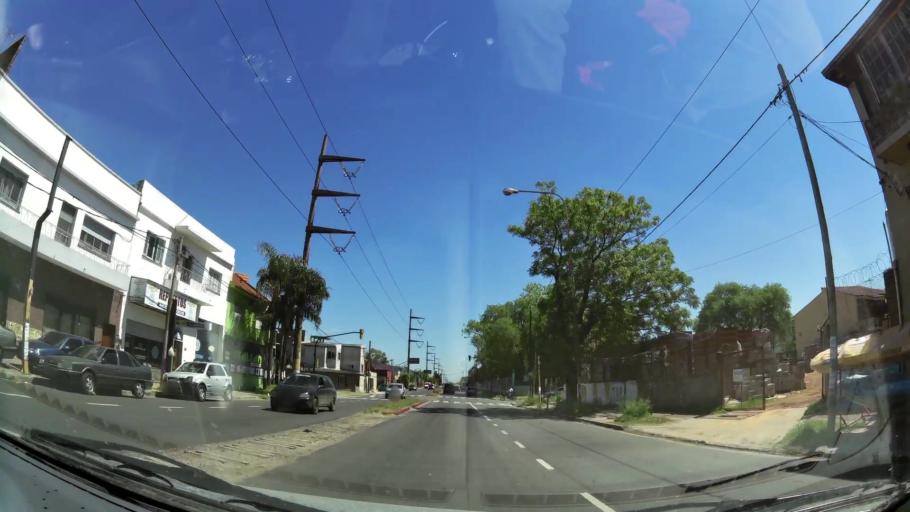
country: AR
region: Buenos Aires
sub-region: Partido de Quilmes
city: Quilmes
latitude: -34.7266
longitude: -58.2850
